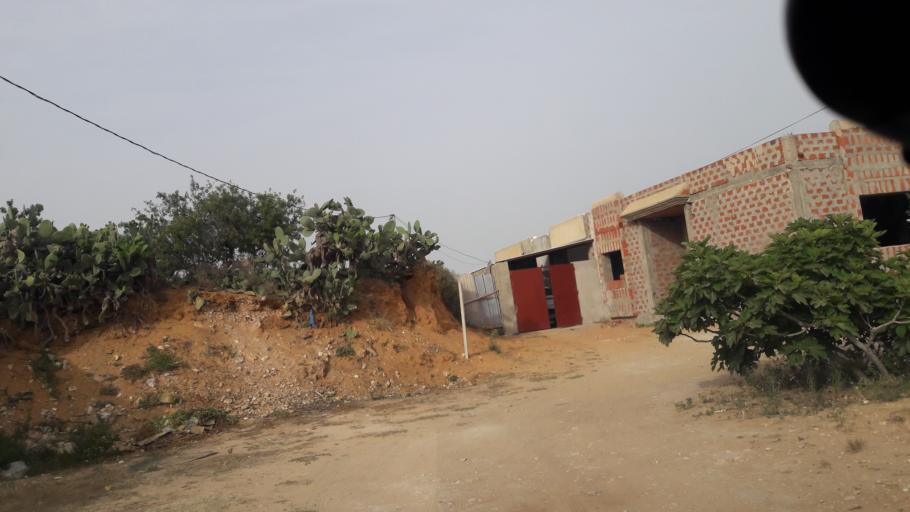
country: TN
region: Safaqis
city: Al Qarmadah
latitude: 34.7809
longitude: 10.7723
